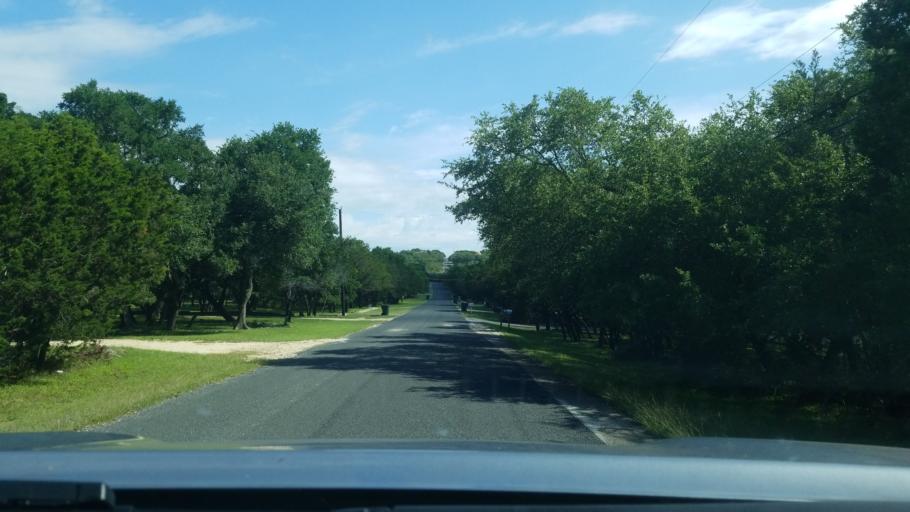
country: US
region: Texas
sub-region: Comal County
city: Bulverde
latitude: 29.7502
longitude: -98.4427
